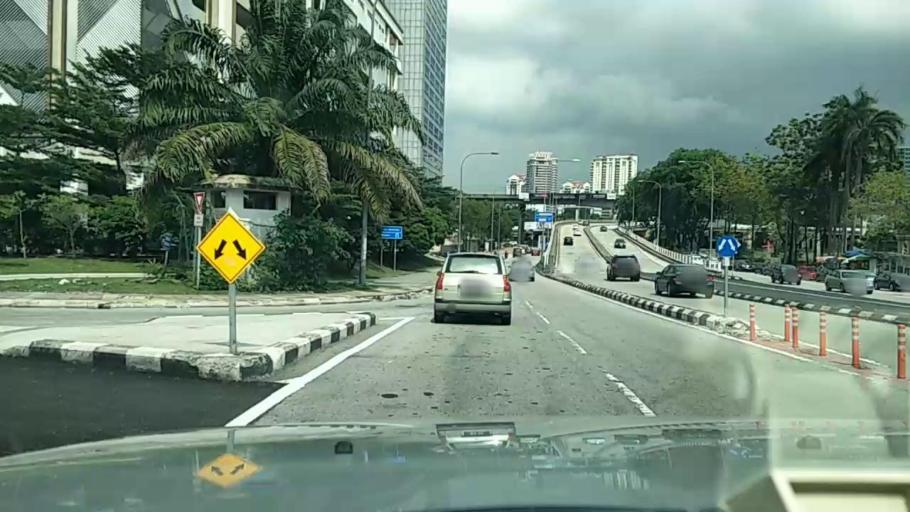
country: MY
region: Kuala Lumpur
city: Kuala Lumpur
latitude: 3.1272
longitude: 101.6760
